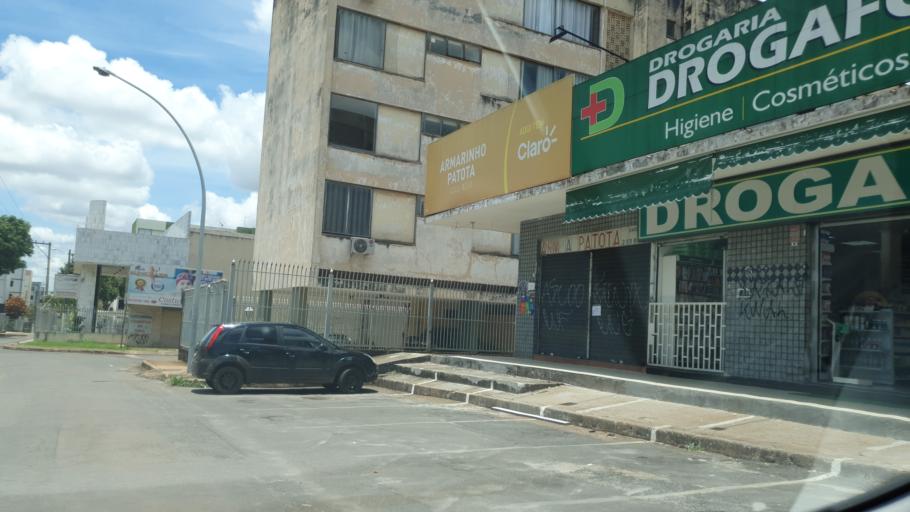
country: BR
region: Federal District
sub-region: Brasilia
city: Brasilia
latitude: -15.7986
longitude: -47.9398
